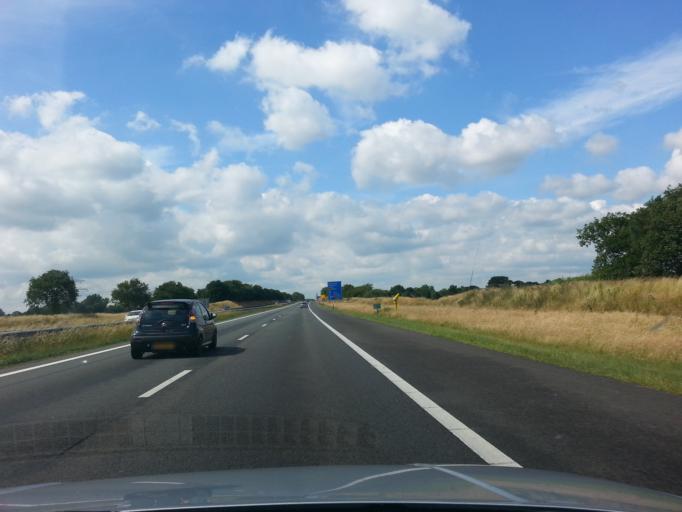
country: NL
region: North Brabant
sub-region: Gemeente Boxmeer
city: Boxmeer
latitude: 51.6538
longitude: 5.9109
